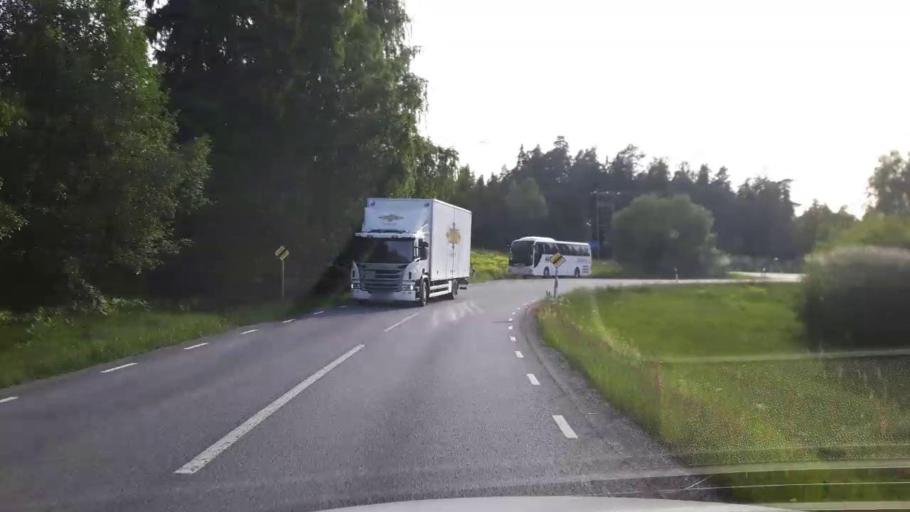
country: SE
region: Uppsala
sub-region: Habo Kommun
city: Balsta
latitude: 59.6255
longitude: 17.4949
